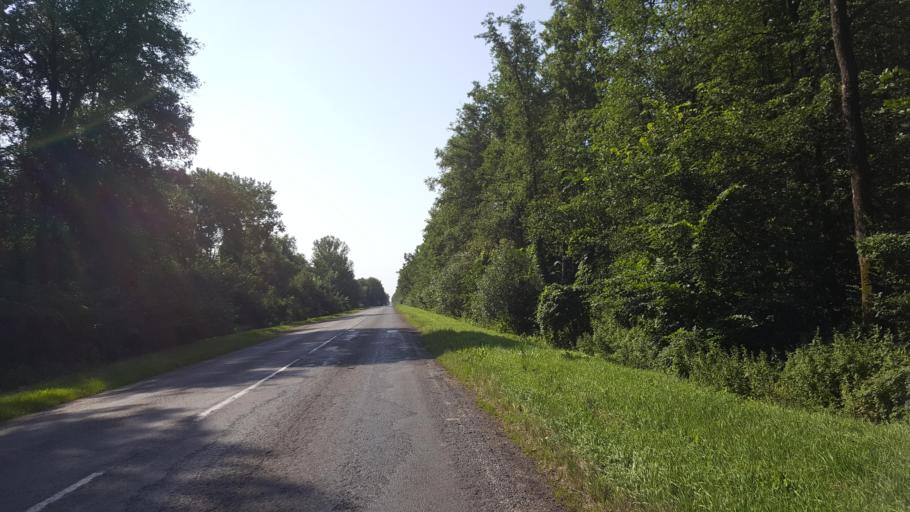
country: BY
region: Brest
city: Zhabinka
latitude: 52.2897
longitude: 23.9419
